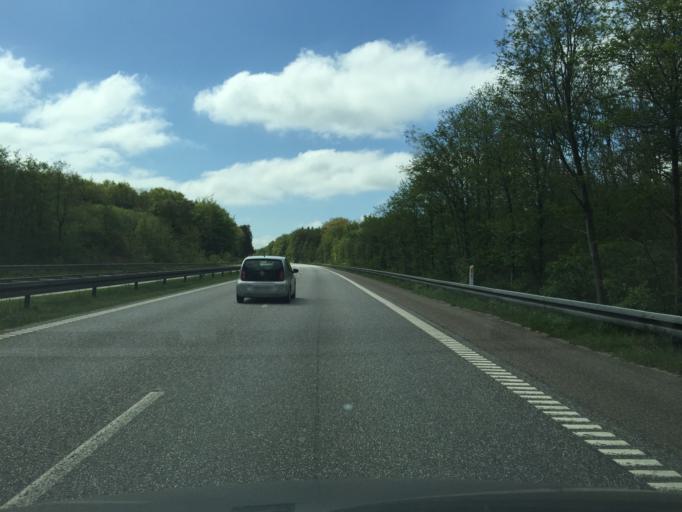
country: DK
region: Zealand
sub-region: Vordingborg Kommune
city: Orslev
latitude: 55.0267
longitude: 11.9858
